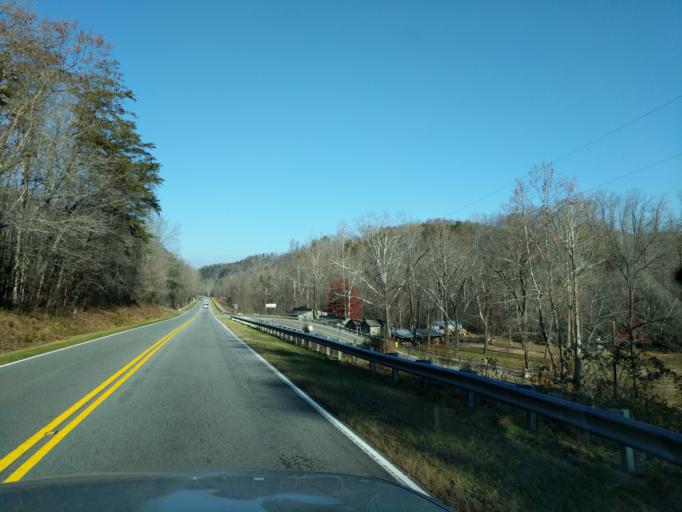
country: US
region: North Carolina
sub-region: McDowell County
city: West Marion
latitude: 35.5628
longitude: -81.9688
